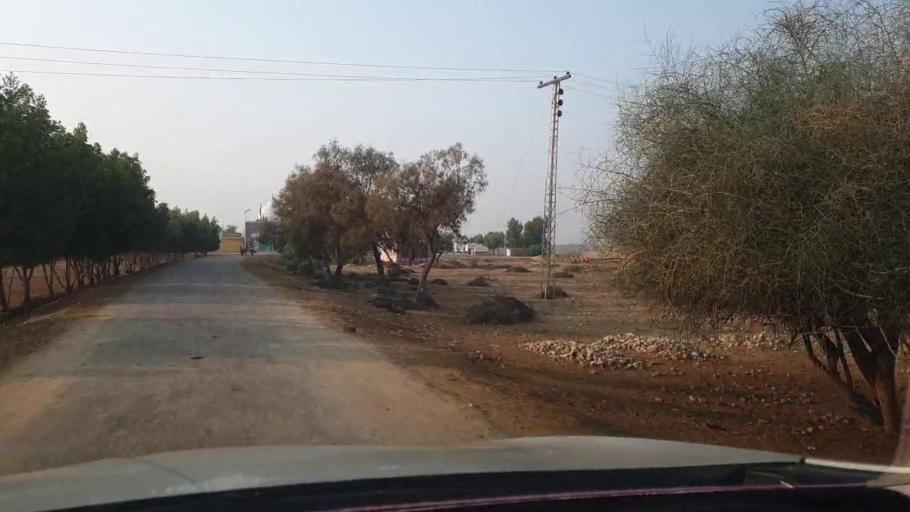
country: PK
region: Sindh
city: Sehwan
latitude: 26.3551
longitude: 67.7624
